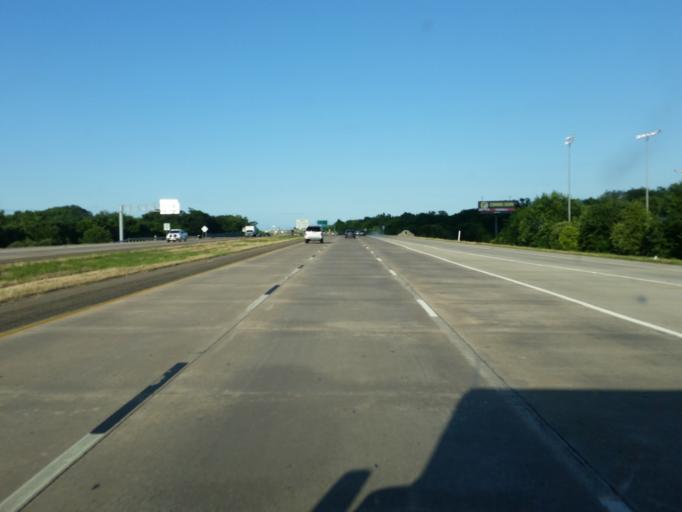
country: US
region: Texas
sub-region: Dallas County
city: Balch Springs
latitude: 32.7018
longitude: -96.6176
